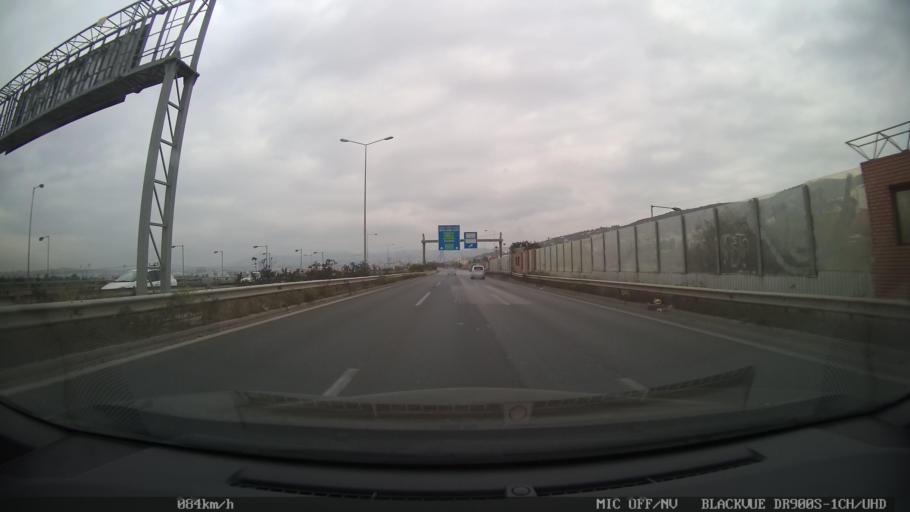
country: GR
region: Central Macedonia
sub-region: Nomos Thessalonikis
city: Polichni
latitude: 40.6737
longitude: 22.9607
